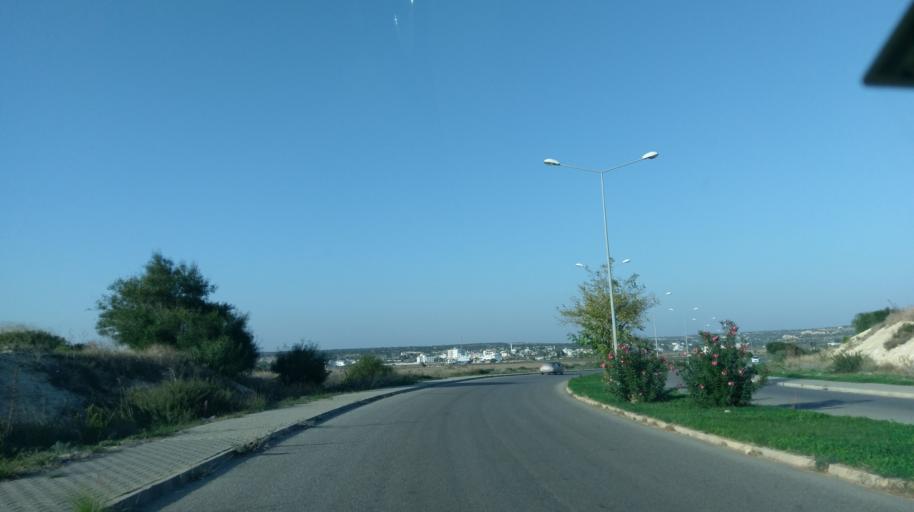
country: CY
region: Ammochostos
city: Leonarisso
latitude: 35.3615
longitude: 34.0709
